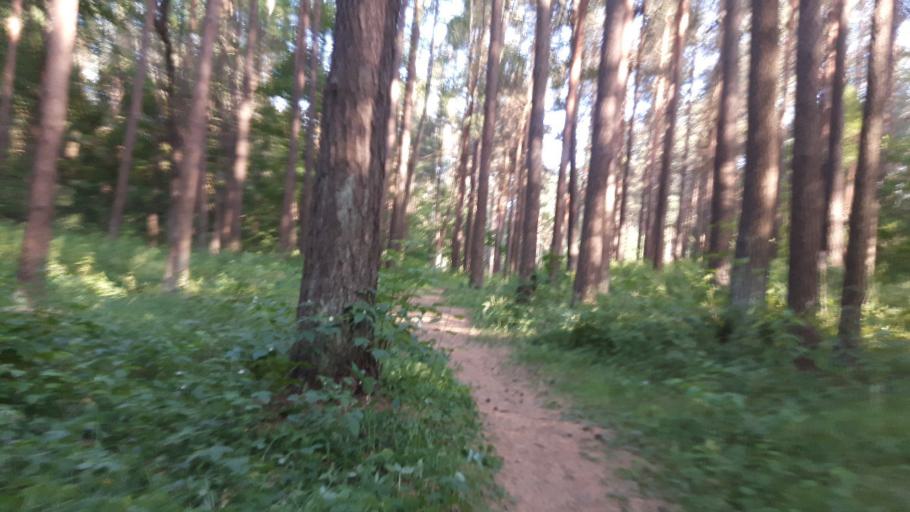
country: LV
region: Riga
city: Jaunciems
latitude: 57.0134
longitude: 24.1343
